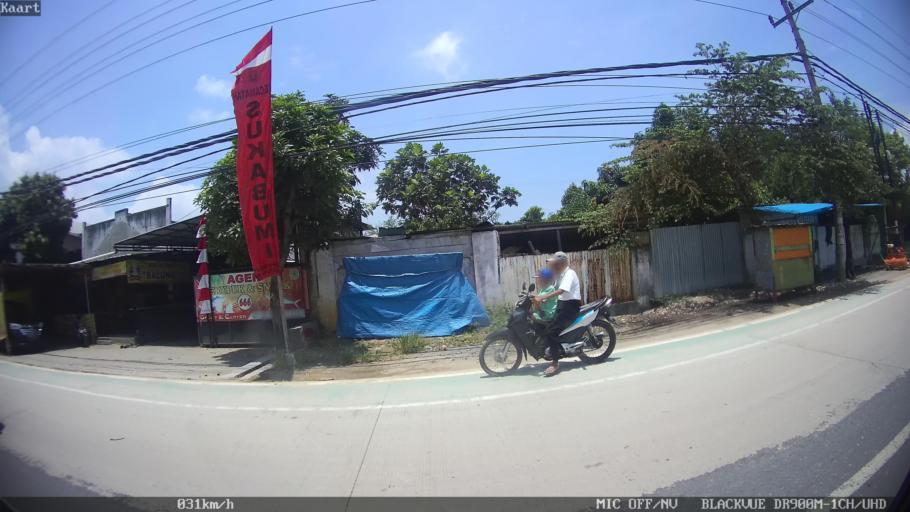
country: ID
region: Lampung
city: Kedaton
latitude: -5.3802
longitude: 105.2911
